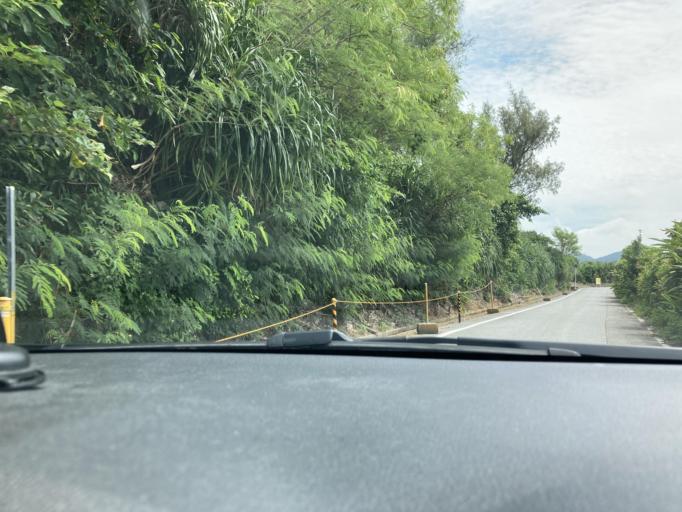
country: JP
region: Okinawa
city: Ishikawa
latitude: 26.4423
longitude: 127.7728
